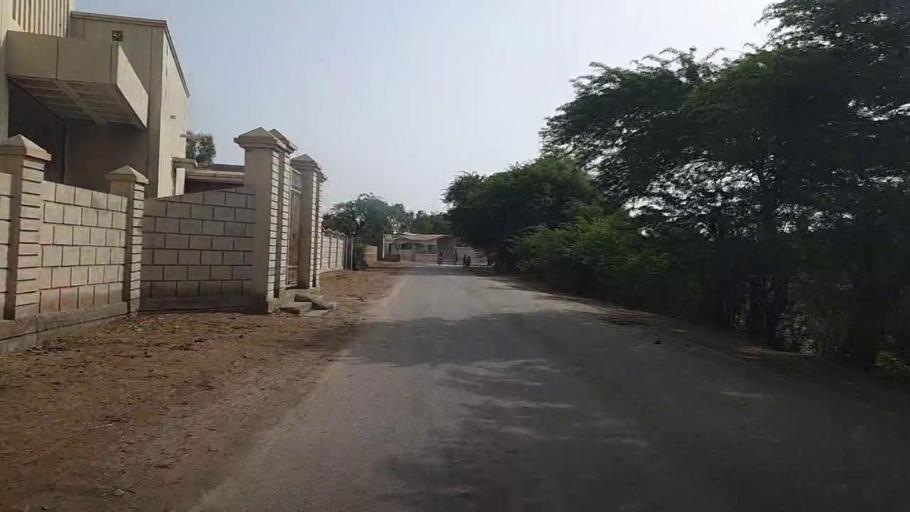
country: PK
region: Sindh
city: Khairpur Nathan Shah
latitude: 27.1087
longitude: 67.7669
